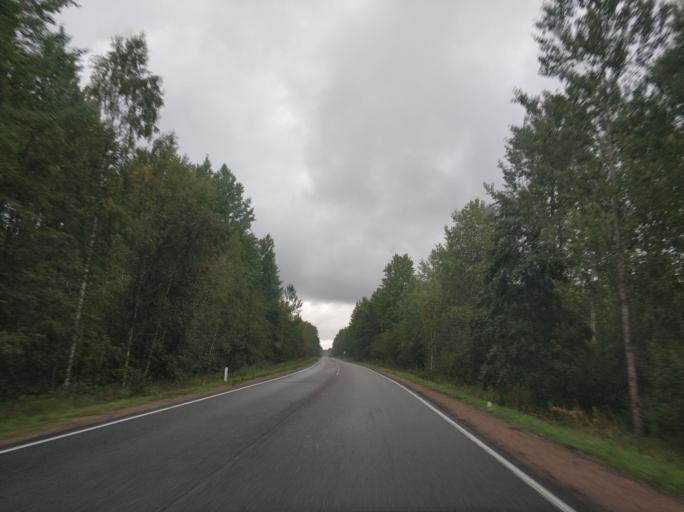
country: RU
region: Leningrad
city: Borisova Griva
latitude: 60.1154
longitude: 30.9637
